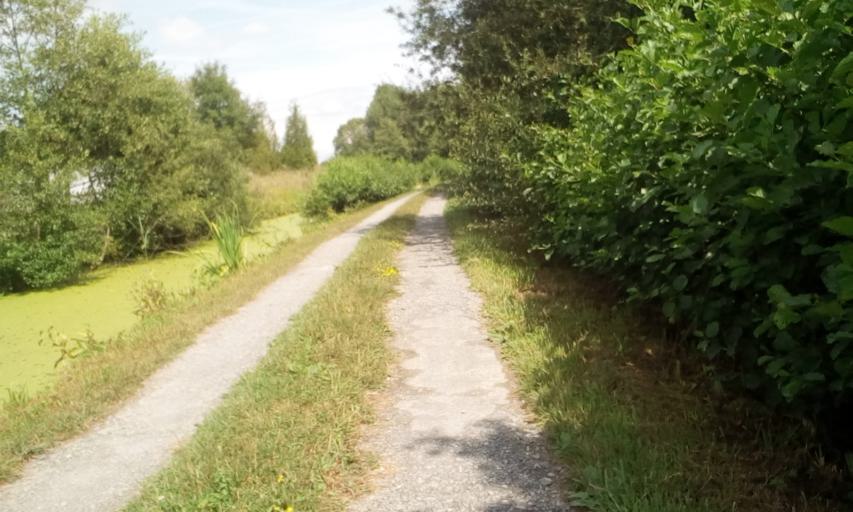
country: FR
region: Lower Normandy
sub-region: Departement du Calvados
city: Bavent
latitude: 49.2398
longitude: -0.1709
